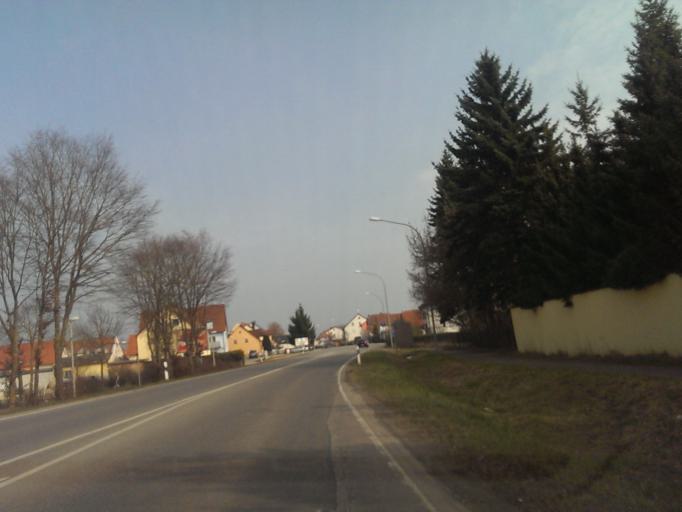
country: DE
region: Bavaria
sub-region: Upper Palatinate
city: Tegernheim
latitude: 49.0244
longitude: 12.1684
